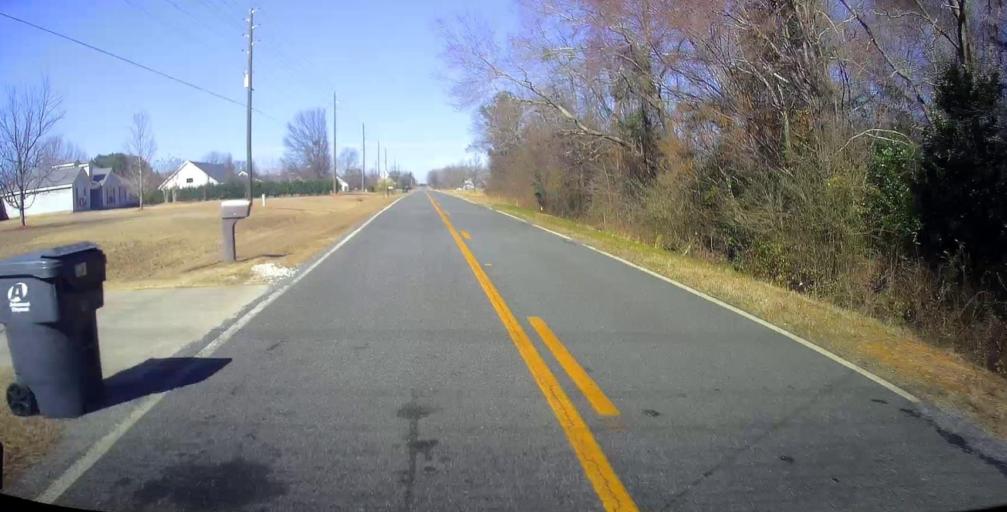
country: US
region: Georgia
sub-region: Peach County
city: Byron
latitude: 32.6205
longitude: -83.7672
